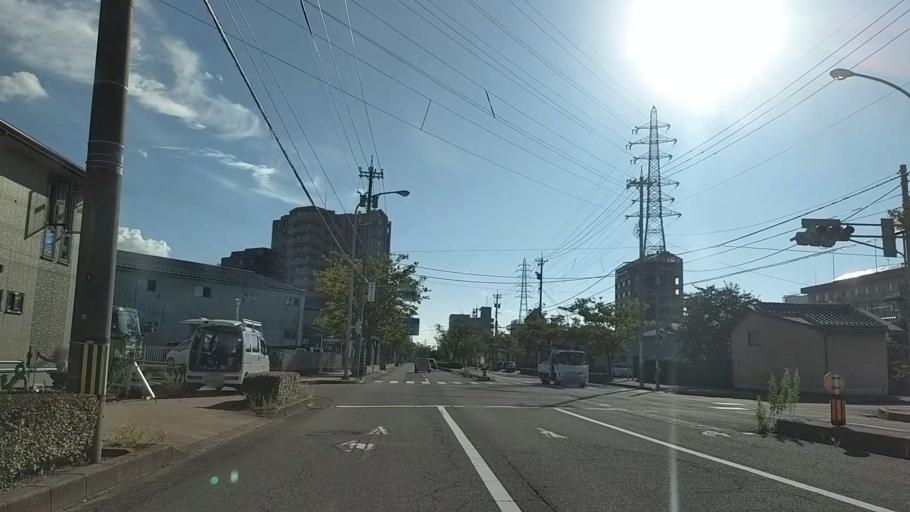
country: JP
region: Ishikawa
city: Kanazawa-shi
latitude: 36.5871
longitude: 136.6397
